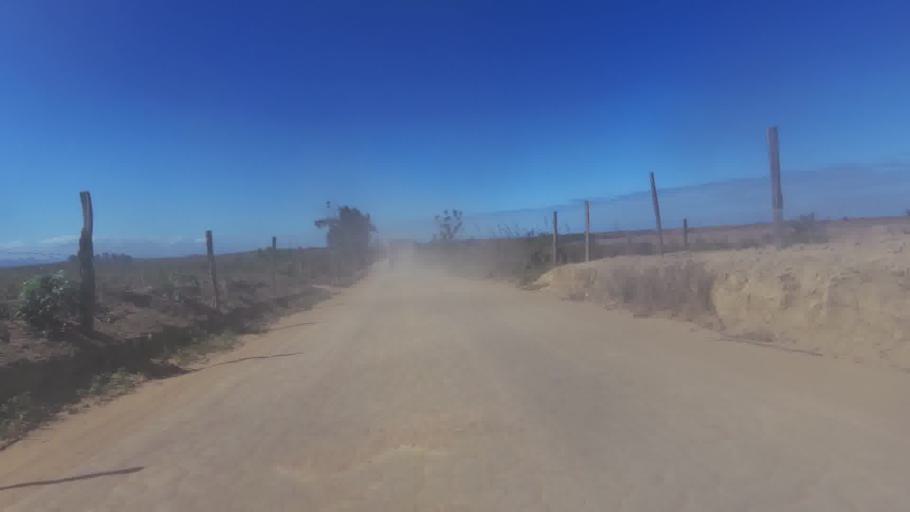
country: BR
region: Espirito Santo
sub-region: Marataizes
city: Marataizes
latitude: -21.1288
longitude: -40.9820
